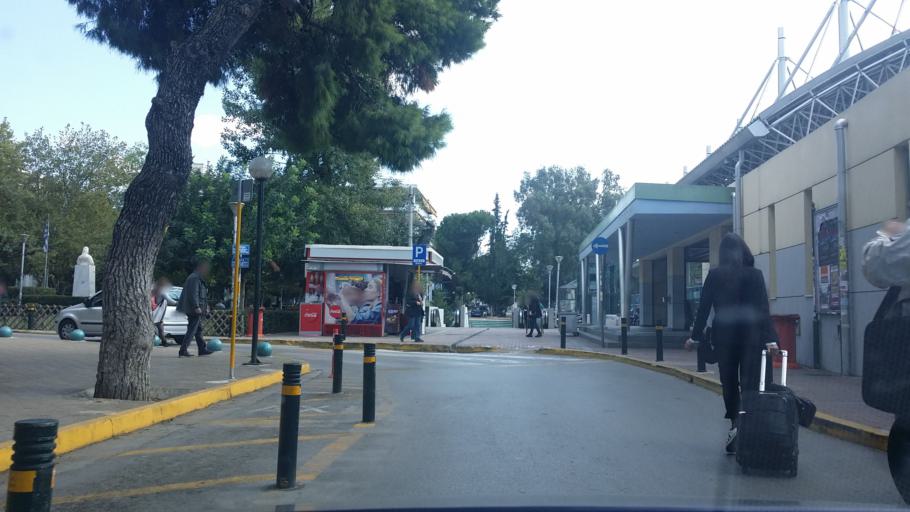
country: GR
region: Attica
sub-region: Nomarchia Athinas
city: Irakleio
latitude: 38.0464
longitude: 23.7660
